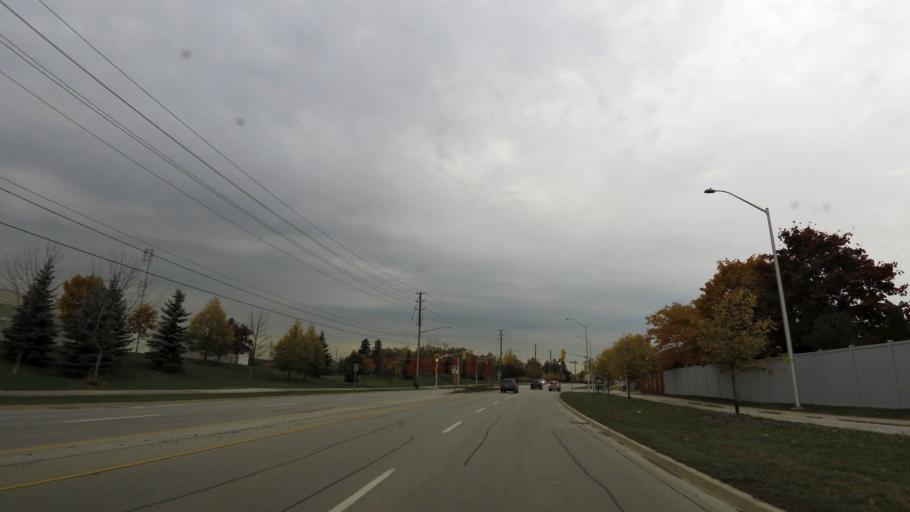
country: CA
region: Ontario
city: Oakville
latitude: 43.4847
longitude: -79.6541
